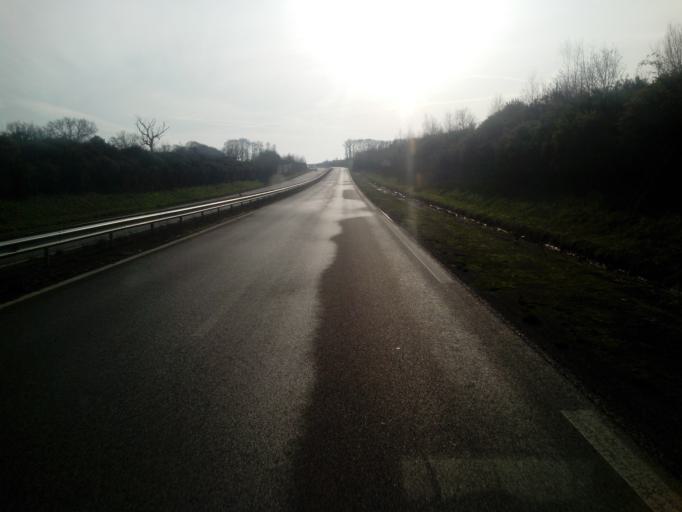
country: FR
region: Brittany
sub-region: Departement d'Ille-et-Vilaine
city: Betton
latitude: 48.1876
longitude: -1.6238
